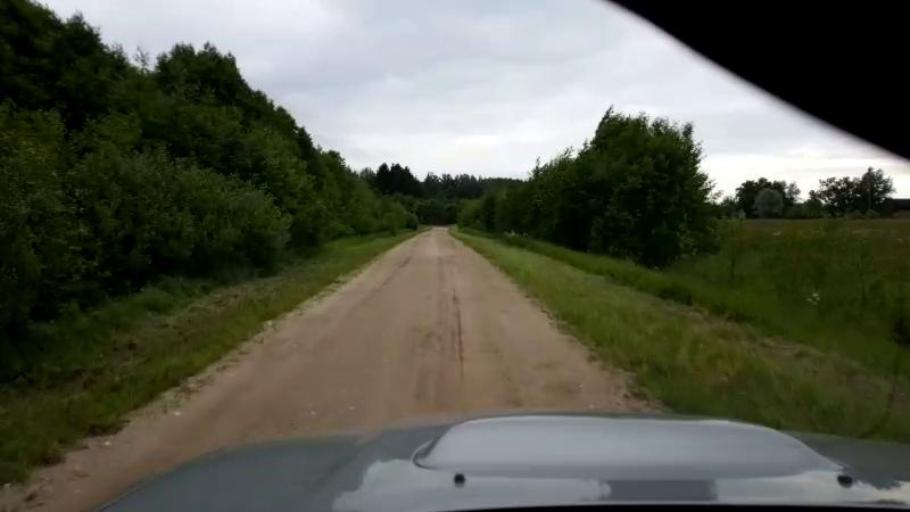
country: EE
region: Paernumaa
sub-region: Halinga vald
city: Parnu-Jaagupi
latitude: 58.5498
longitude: 24.5769
